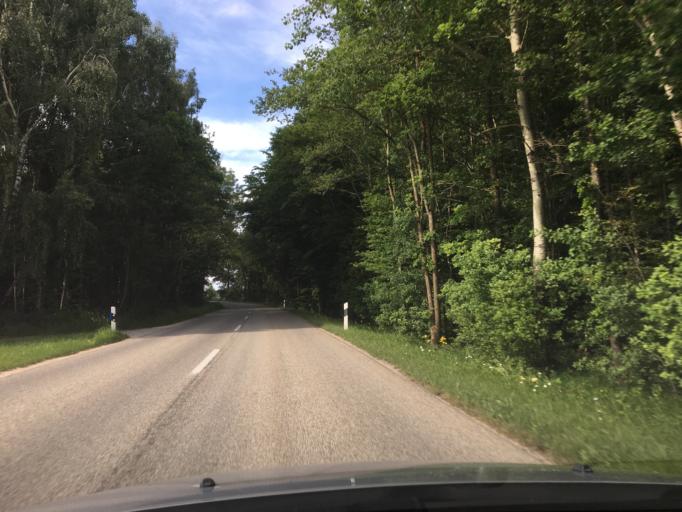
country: DE
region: Bavaria
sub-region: Upper Bavaria
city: Niedertaufkirchen
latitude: 48.3448
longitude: 12.5722
